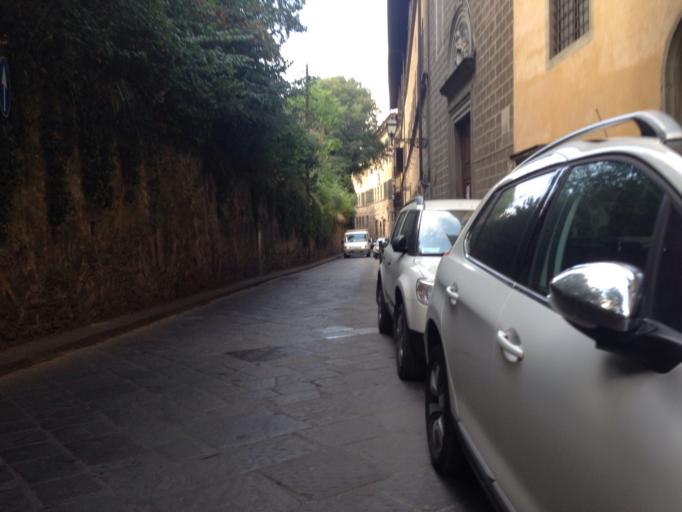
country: IT
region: Tuscany
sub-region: Province of Florence
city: Florence
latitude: 43.7654
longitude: 11.2569
